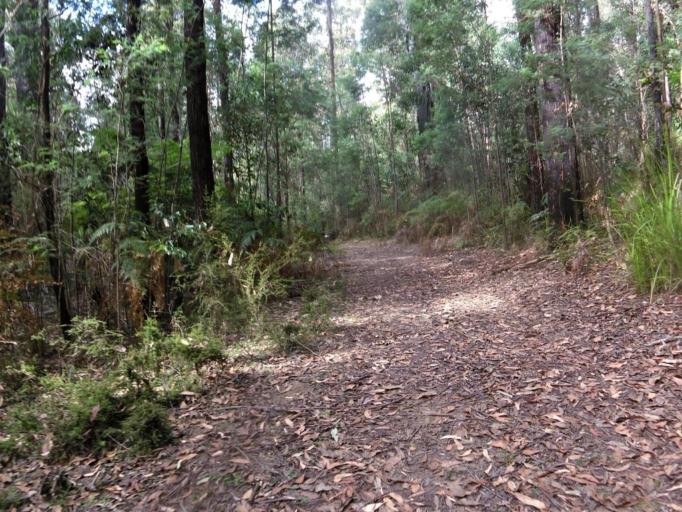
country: AU
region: Victoria
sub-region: Murrindindi
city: Alexandra
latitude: -37.3935
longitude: 145.5831
